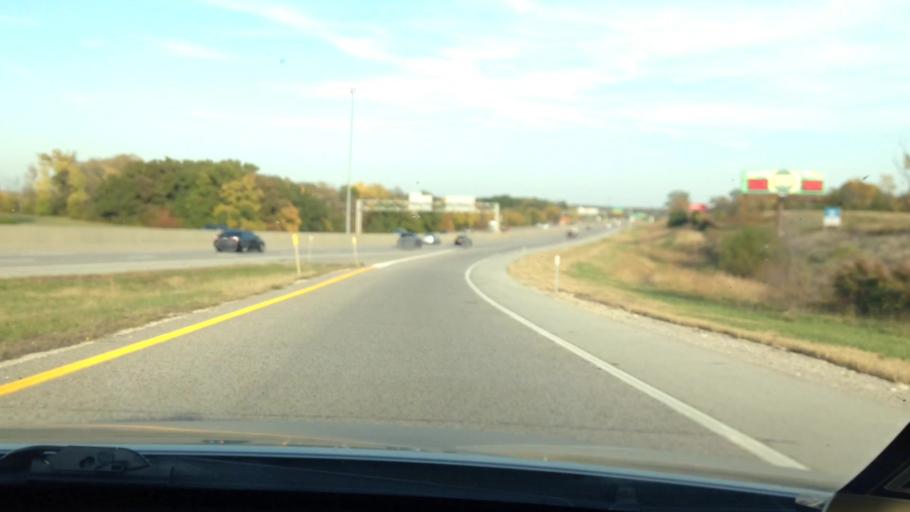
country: US
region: Kansas
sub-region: Wyandotte County
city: Edwardsville
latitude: 39.1058
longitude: -94.8330
